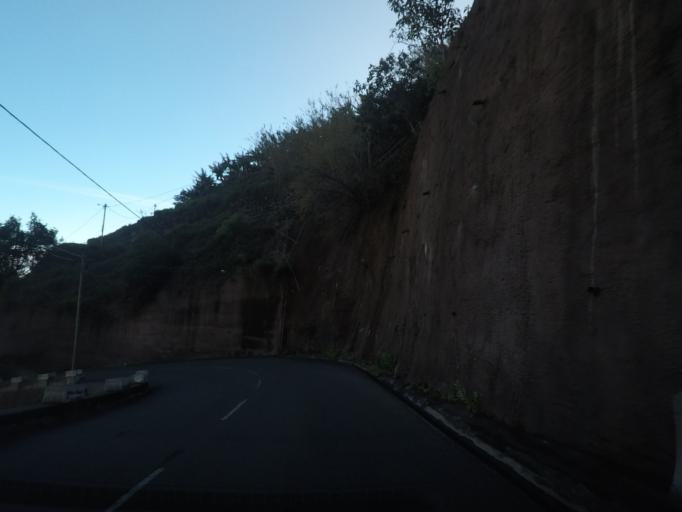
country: PT
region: Madeira
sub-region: Calheta
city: Arco da Calheta
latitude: 32.7089
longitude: -17.1355
